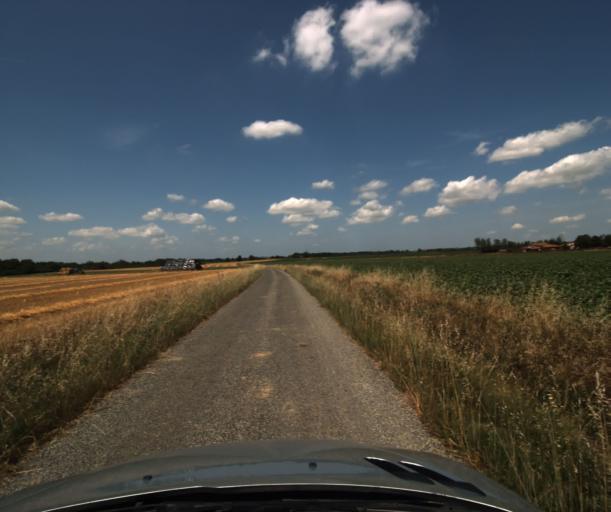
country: FR
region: Midi-Pyrenees
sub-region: Departement de la Haute-Garonne
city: Labastidette
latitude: 43.4725
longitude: 1.2048
